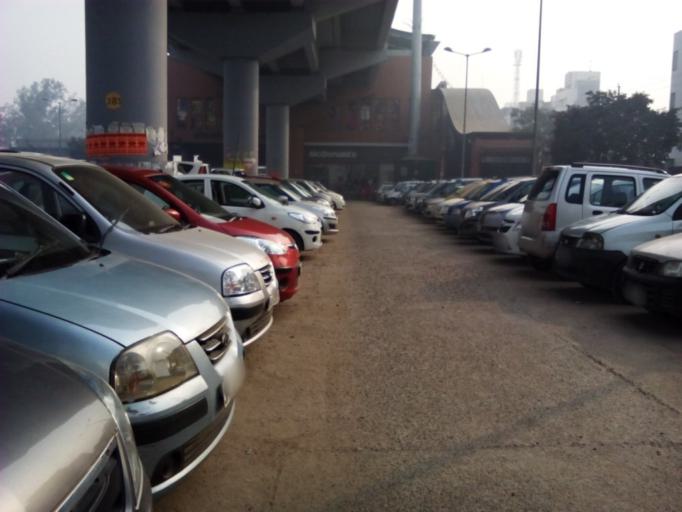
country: IN
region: Uttar Pradesh
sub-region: Gautam Buddha Nagar
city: Noida
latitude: 28.6454
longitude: 77.3233
